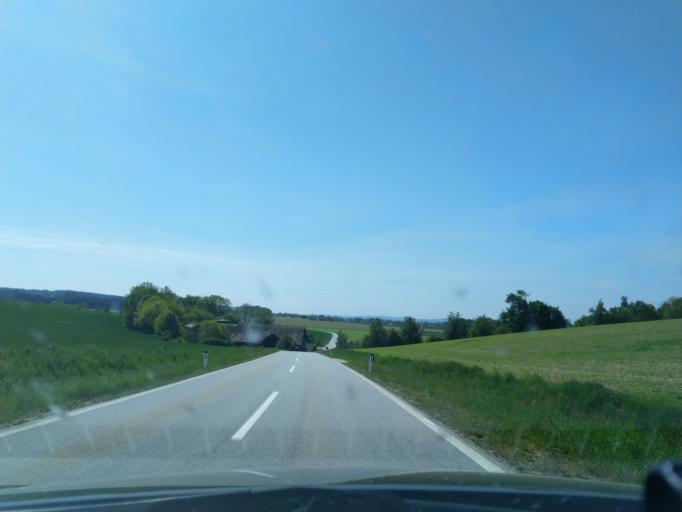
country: DE
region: Bavaria
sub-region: Lower Bavaria
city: Bad Fussing
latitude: 48.2687
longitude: 13.3418
